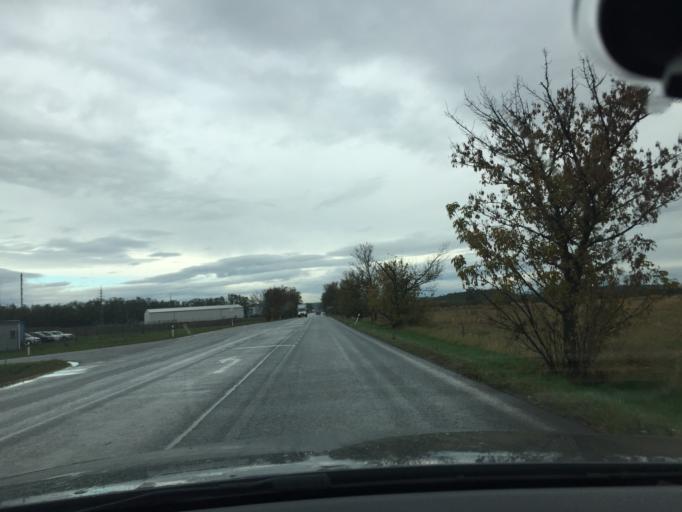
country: CZ
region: Central Bohemia
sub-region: Okres Melnik
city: Veltrusy
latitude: 50.2541
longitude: 14.3509
